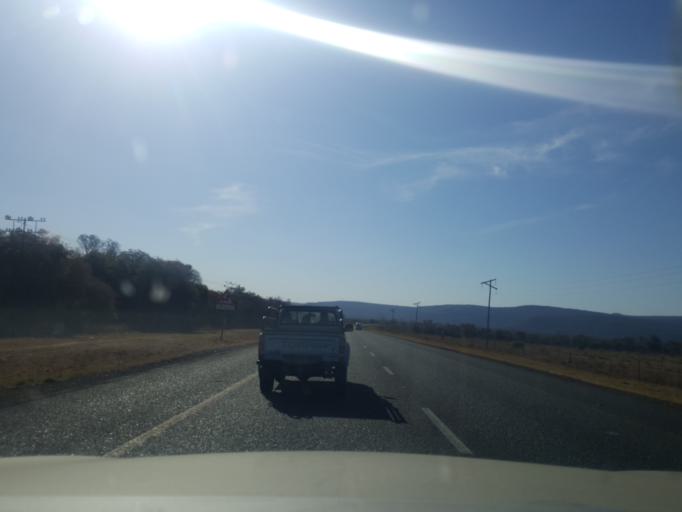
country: ZA
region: North-West
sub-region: Ngaka Modiri Molema District Municipality
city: Zeerust
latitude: -25.5368
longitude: 26.1944
